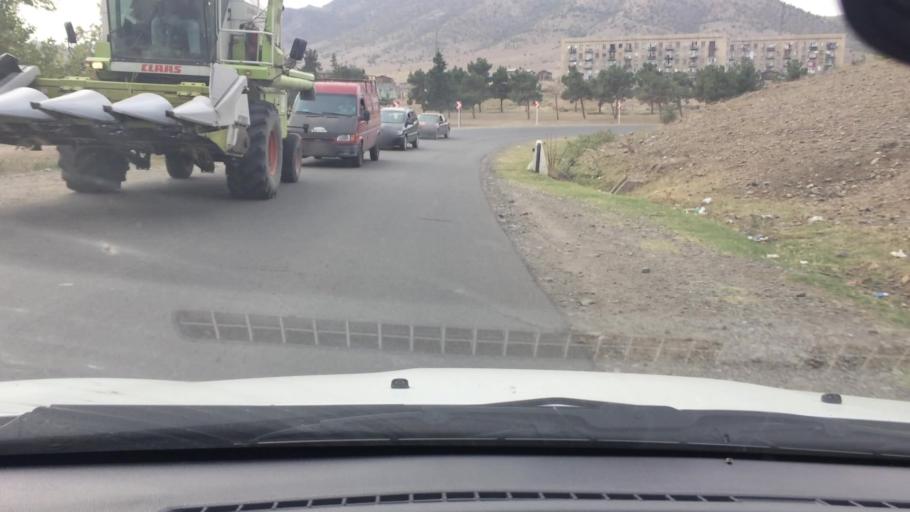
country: GE
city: Naghvarevi
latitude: 41.3604
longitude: 44.8379
